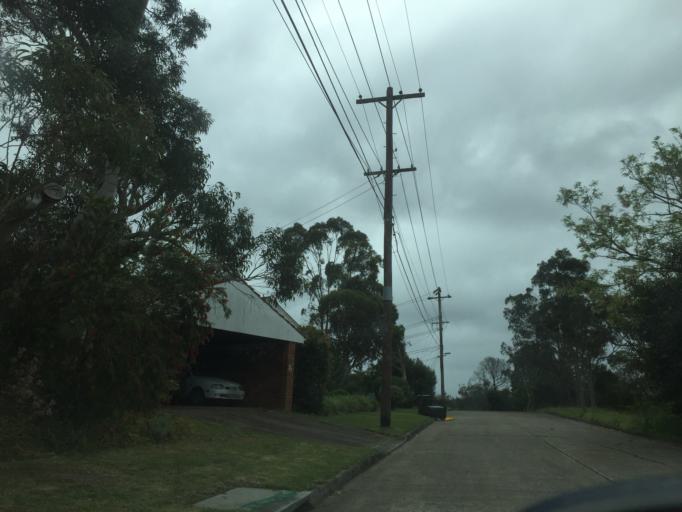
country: AU
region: New South Wales
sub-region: Willoughby
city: Lane Cove North
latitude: -33.8016
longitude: 151.1604
